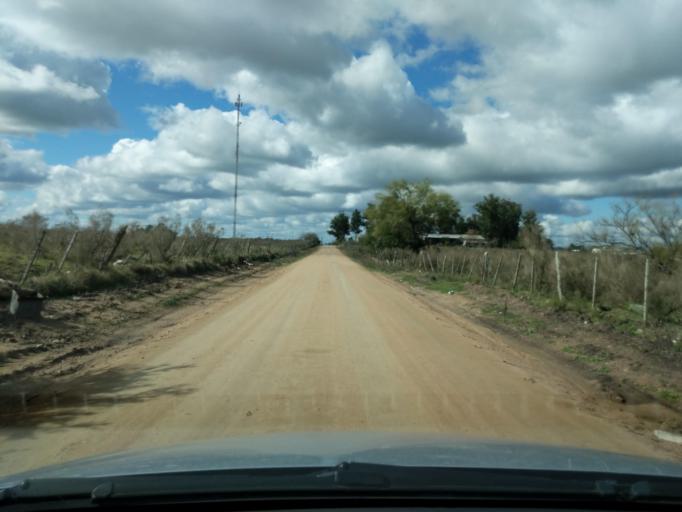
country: UY
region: Florida
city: Florida
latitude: -34.0856
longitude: -56.2355
